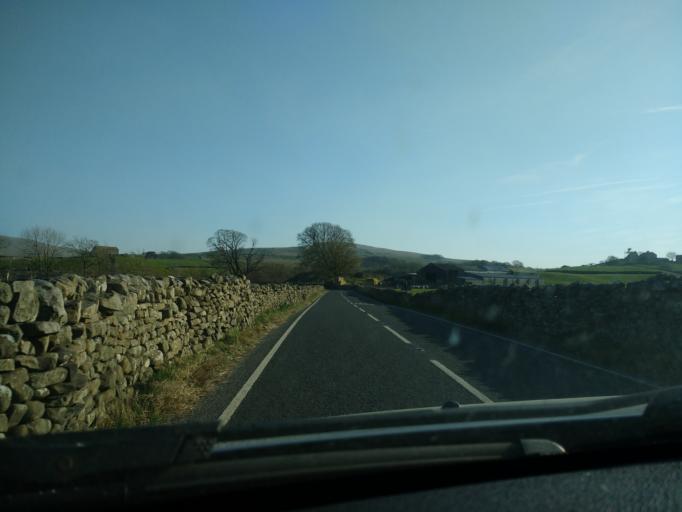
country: GB
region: England
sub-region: Cumbria
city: Kirkby Stephen
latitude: 54.3133
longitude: -2.2203
